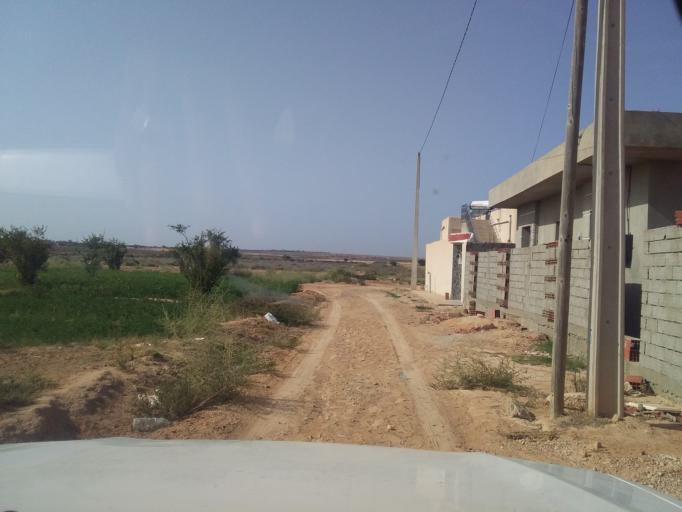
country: TN
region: Qabis
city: Gabes
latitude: 33.6430
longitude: 10.2951
